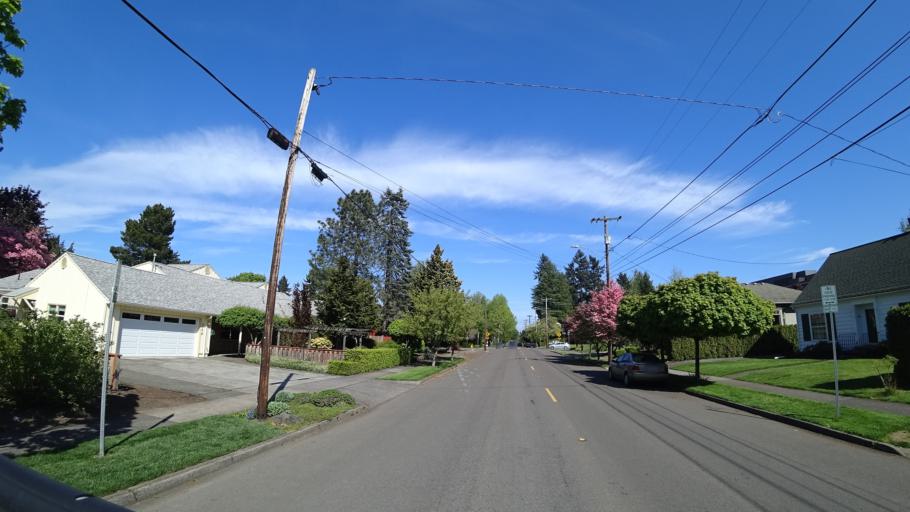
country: US
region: Oregon
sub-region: Washington County
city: Hillsboro
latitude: 45.5225
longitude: -122.9781
